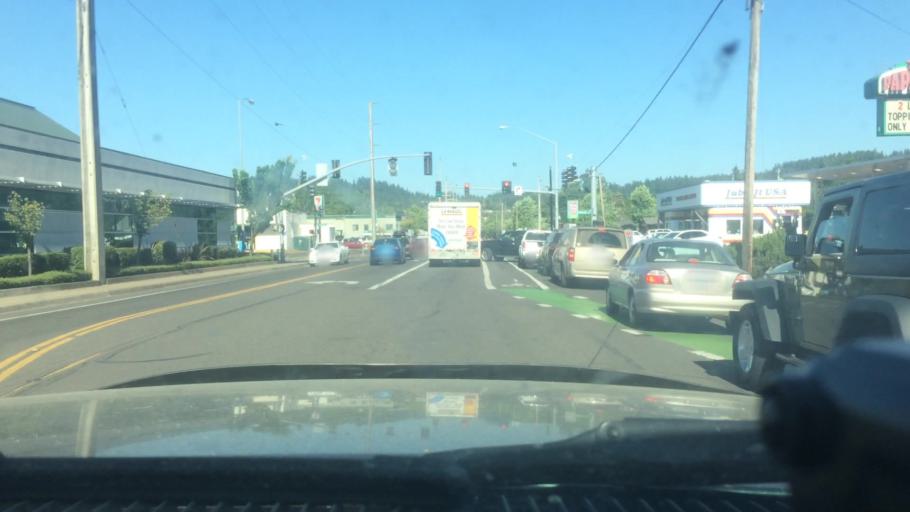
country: US
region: Oregon
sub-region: Lane County
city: Eugene
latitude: 44.0262
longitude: -123.0916
